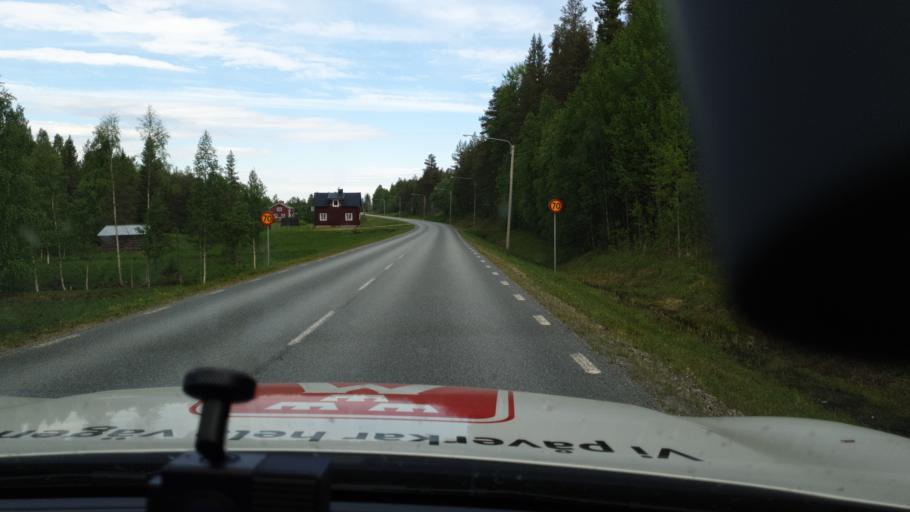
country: SE
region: Vaesterbotten
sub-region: Lycksele Kommun
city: Soderfors
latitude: 65.1108
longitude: 18.3016
